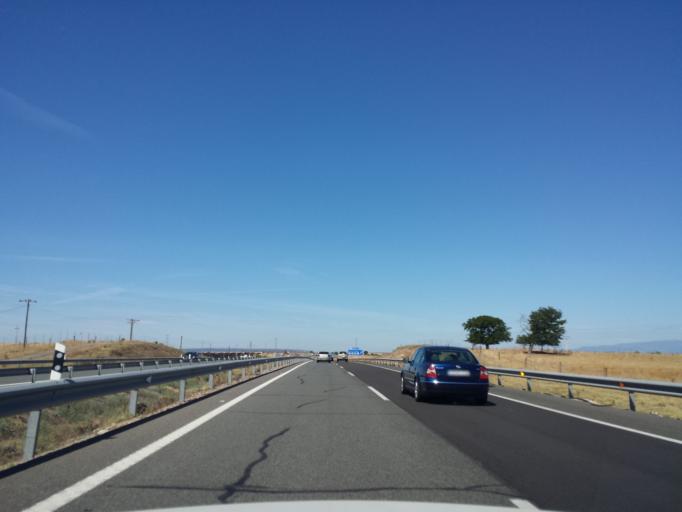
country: ES
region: Castille-La Mancha
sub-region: Province of Toledo
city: Caleruela
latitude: 39.8952
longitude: -5.3123
